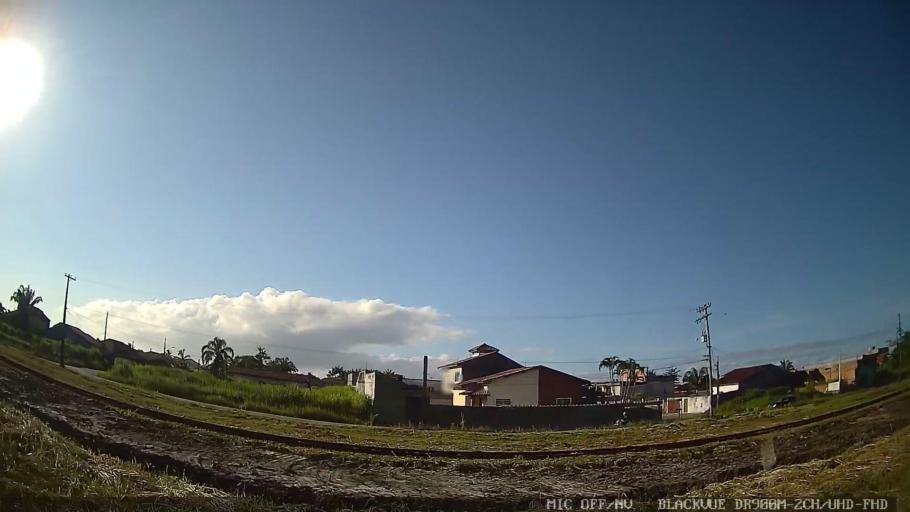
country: BR
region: Sao Paulo
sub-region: Peruibe
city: Peruibe
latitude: -24.2765
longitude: -46.9543
